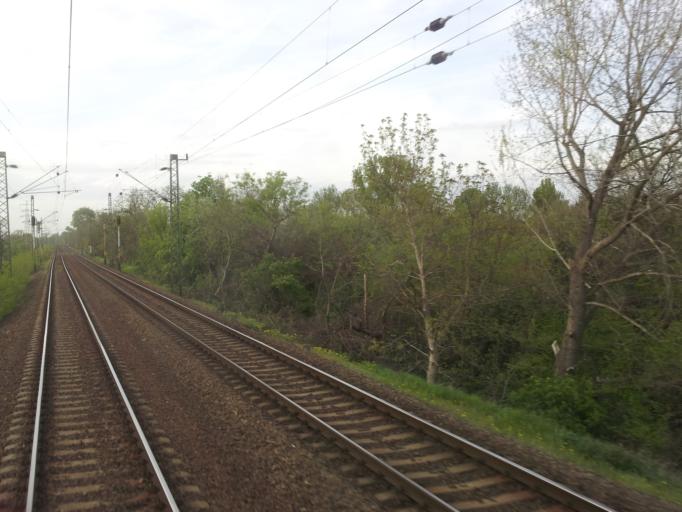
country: HU
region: Budapest
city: Budapest X. keruelet
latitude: 47.4973
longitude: 19.1589
